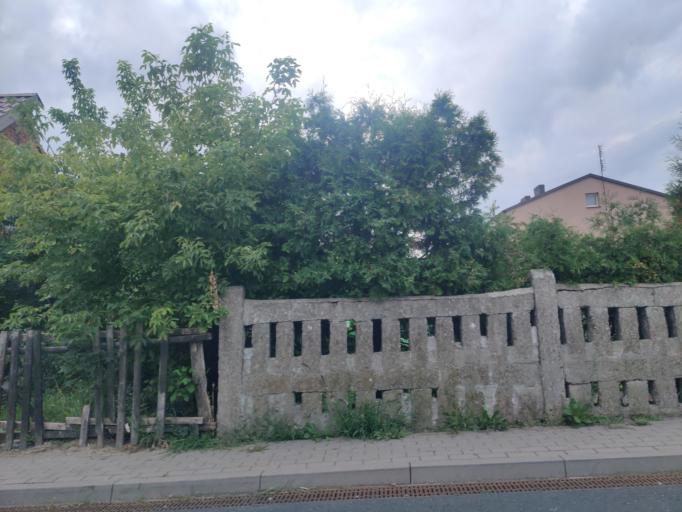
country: PL
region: Greater Poland Voivodeship
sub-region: Konin
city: Konin
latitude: 52.1959
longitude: 18.3054
